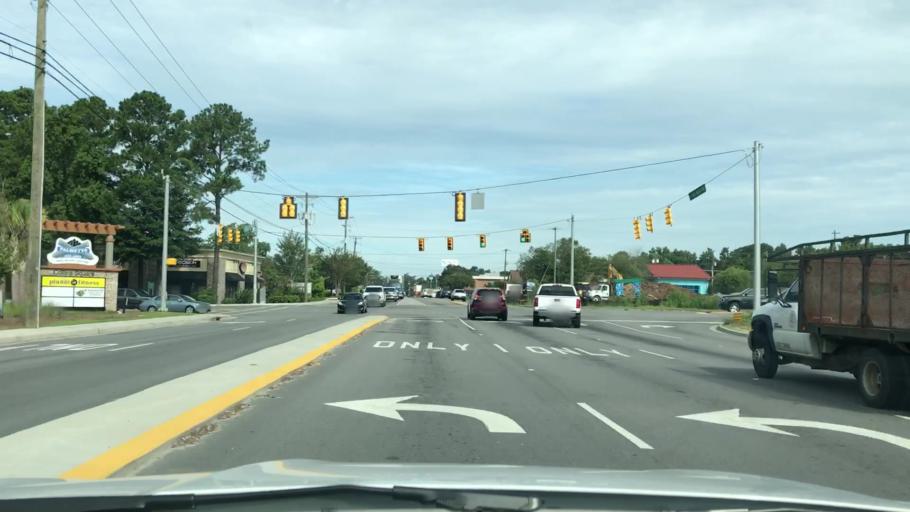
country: US
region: South Carolina
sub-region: Dorchester County
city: Summerville
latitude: 33.0235
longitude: -80.1651
